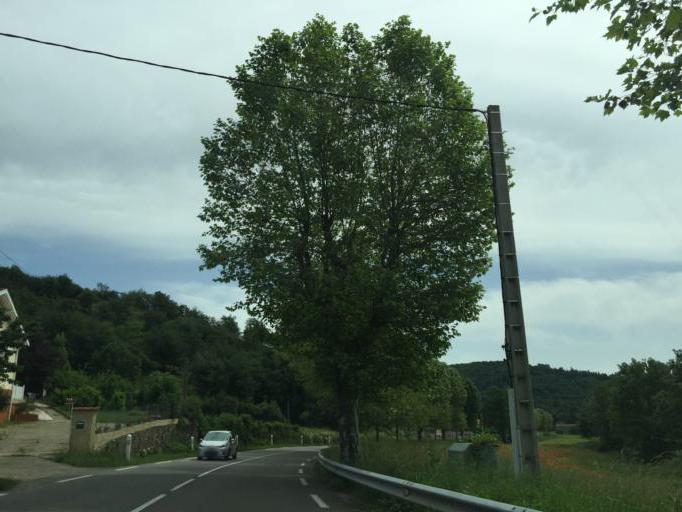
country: FR
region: Rhone-Alpes
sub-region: Departement de l'Ardeche
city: Saint-Marcel-les-Annonay
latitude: 45.2929
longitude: 4.6163
